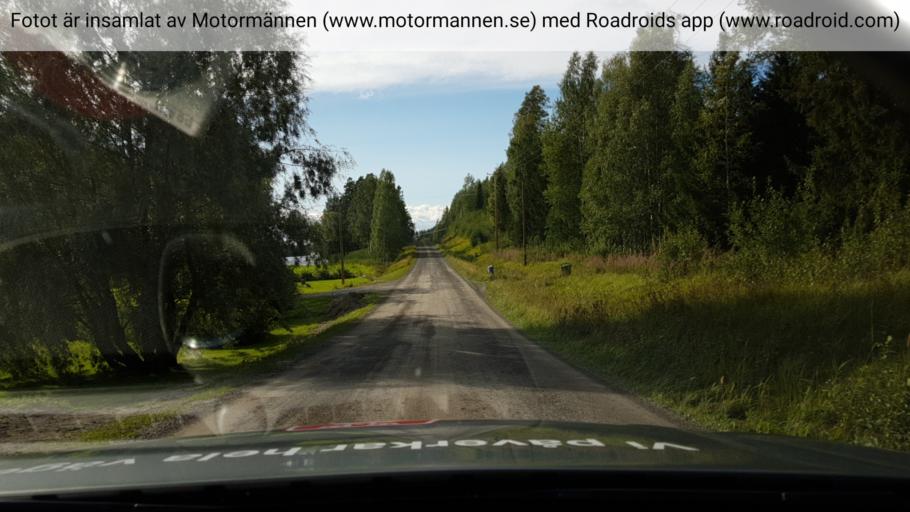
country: SE
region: Jaemtland
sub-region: Braecke Kommun
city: Braecke
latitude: 63.1961
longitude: 15.4875
